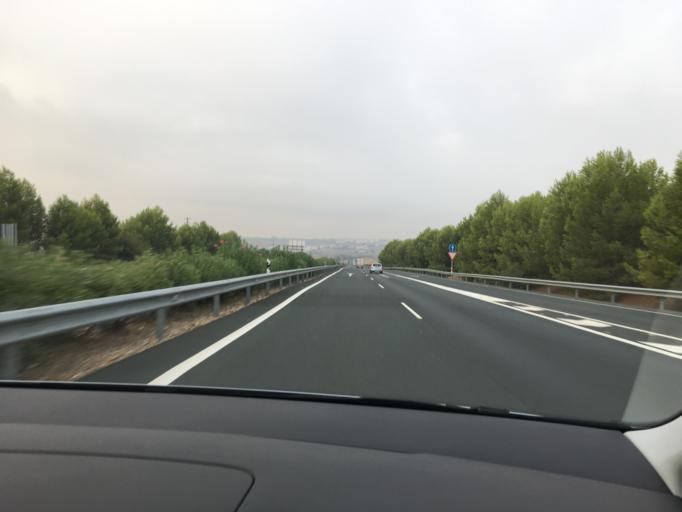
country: ES
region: Andalusia
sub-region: Province of Cordoba
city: La Carlota
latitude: 37.6957
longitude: -4.9194
